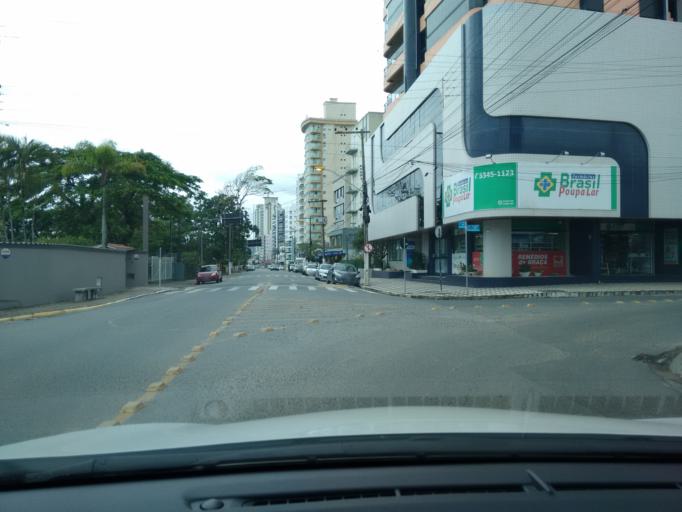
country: BR
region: Santa Catarina
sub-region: Penha
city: Penha
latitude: -26.7578
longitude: -48.6755
